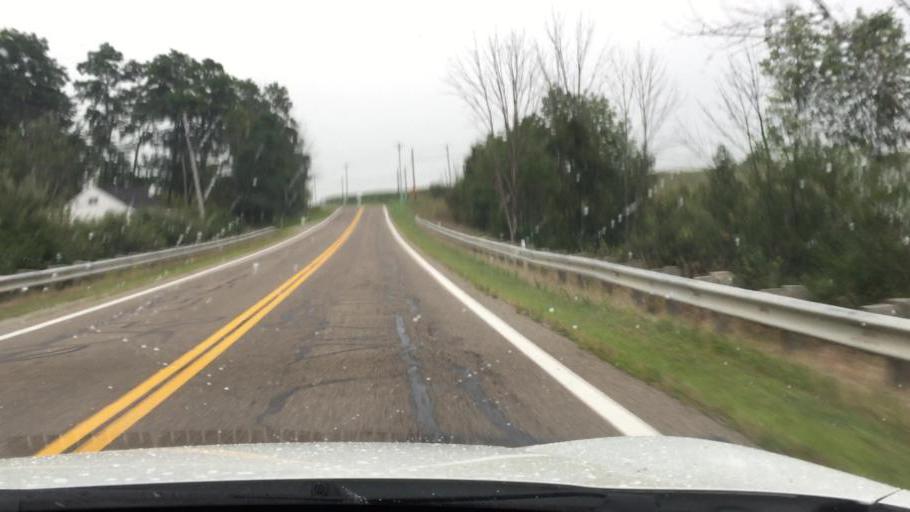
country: US
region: Ohio
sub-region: Champaign County
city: Mechanicsburg
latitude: 40.0150
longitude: -83.6313
